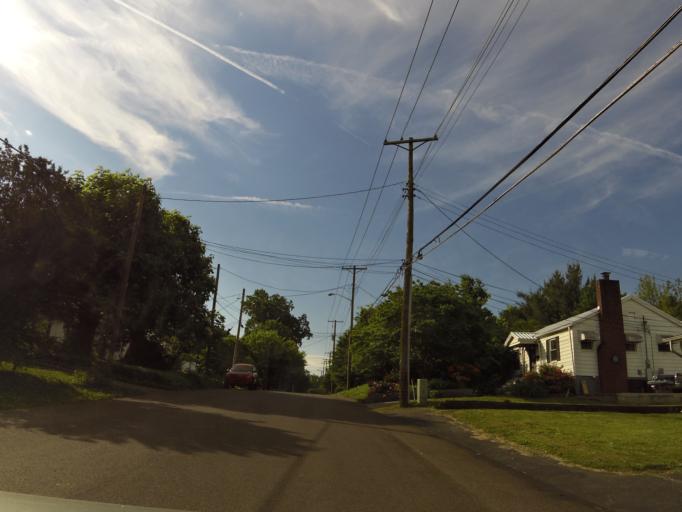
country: US
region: Tennessee
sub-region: Knox County
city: Knoxville
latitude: 36.0004
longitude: -83.9193
